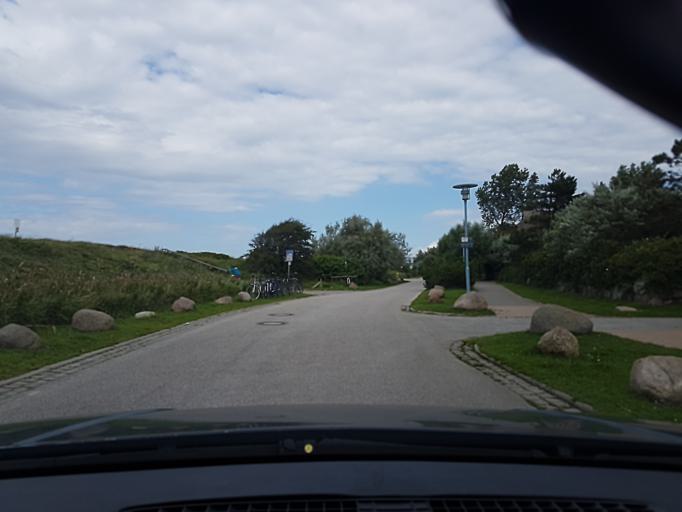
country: DE
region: Mecklenburg-Vorpommern
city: Ostseebad Dierhagen
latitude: 54.3524
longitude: 12.3881
